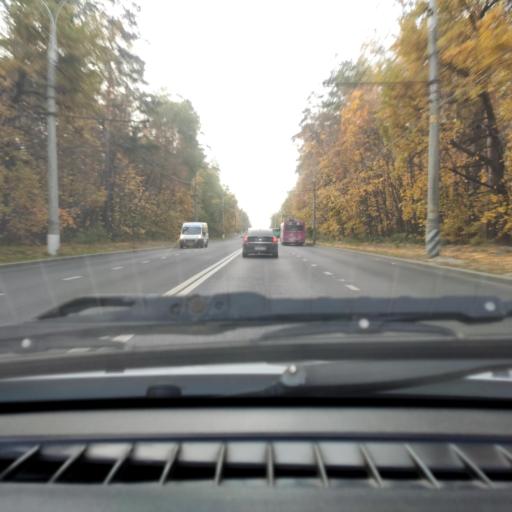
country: RU
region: Samara
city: Zhigulevsk
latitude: 53.4979
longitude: 49.4632
